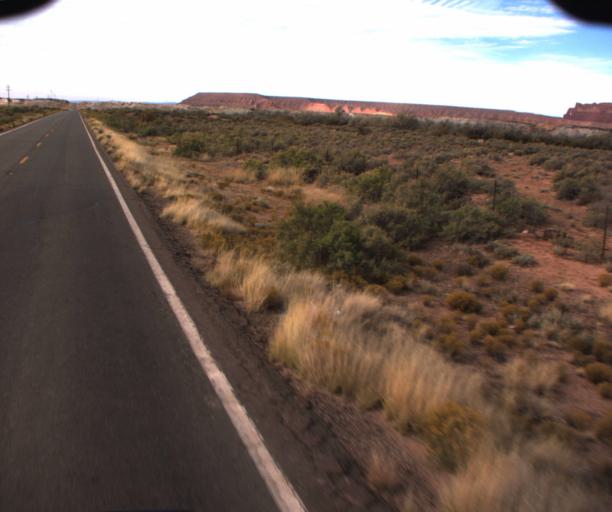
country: US
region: Arizona
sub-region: Apache County
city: Many Farms
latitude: 36.4966
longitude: -109.4887
